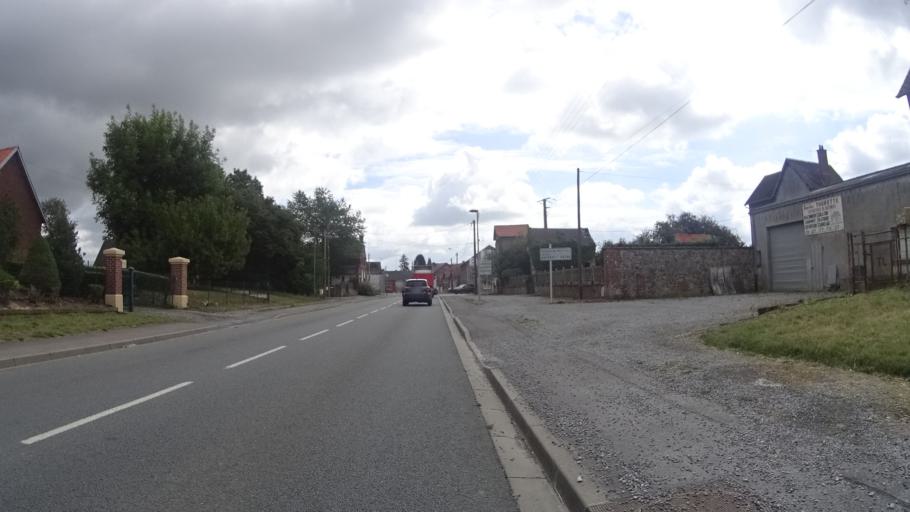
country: FR
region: Nord-Pas-de-Calais
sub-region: Departement du Nord
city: Landrecies
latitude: 50.1187
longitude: 3.7023
